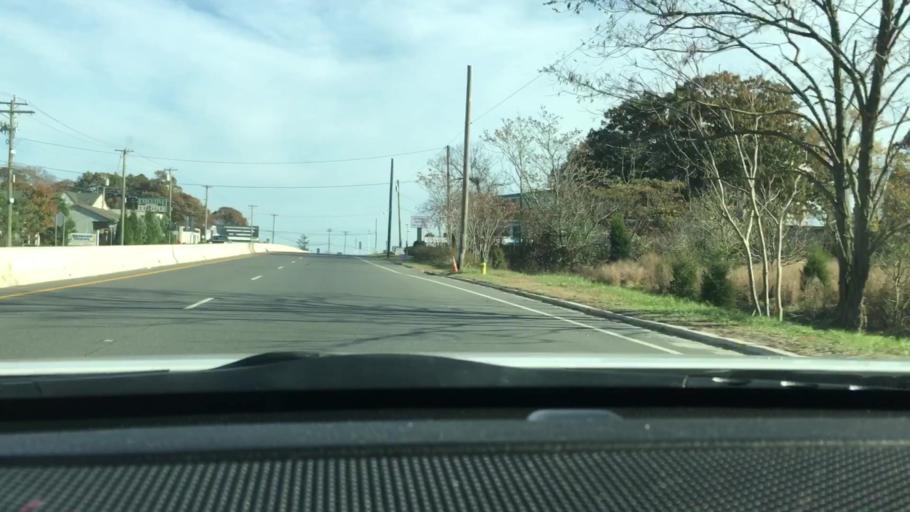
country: US
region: New Jersey
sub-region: Atlantic County
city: Absecon
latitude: 39.4191
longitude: -74.4955
